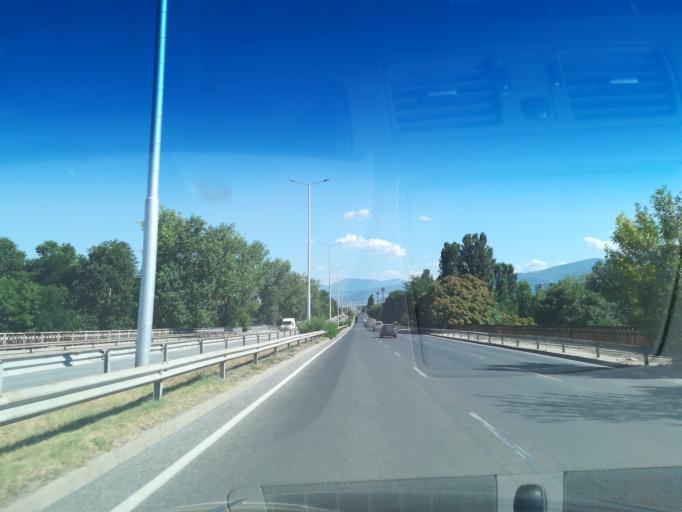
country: BG
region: Plovdiv
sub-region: Obshtina Plovdiv
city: Plovdiv
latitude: 42.1149
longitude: 24.7779
